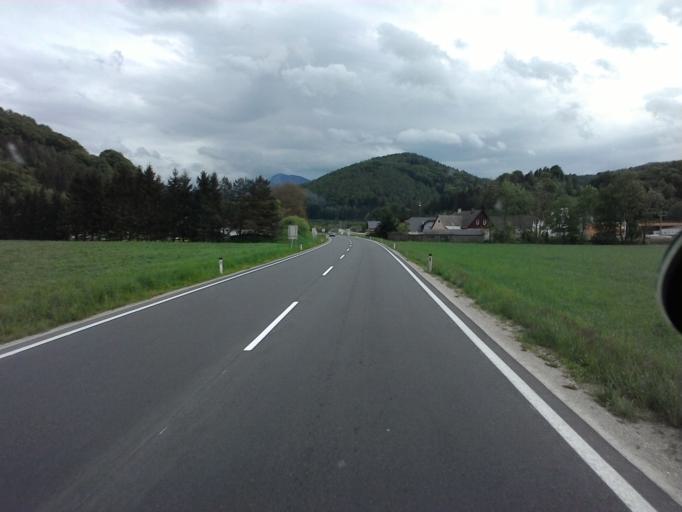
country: AT
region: Upper Austria
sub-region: Politischer Bezirk Kirchdorf an der Krems
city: Micheldorf in Oberoesterreich
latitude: 47.8736
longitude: 14.1316
